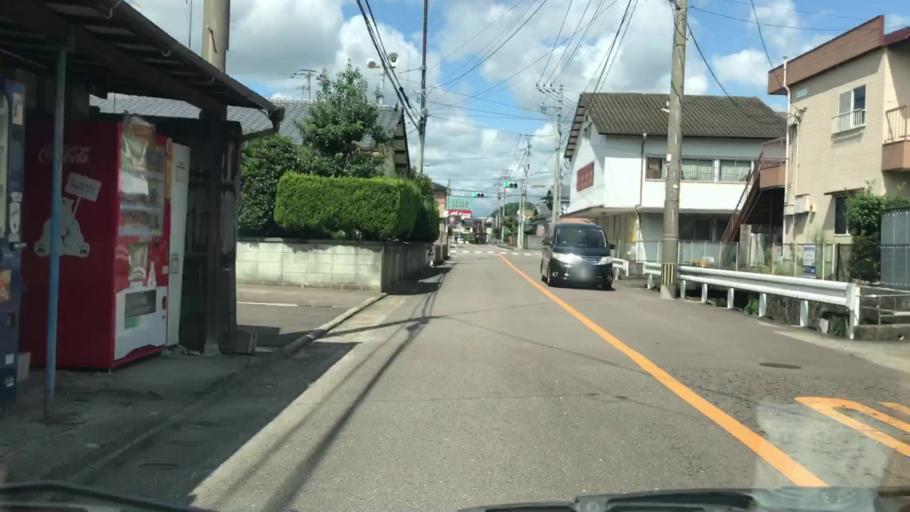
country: JP
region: Saga Prefecture
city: Saga-shi
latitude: 33.2455
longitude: 130.2031
